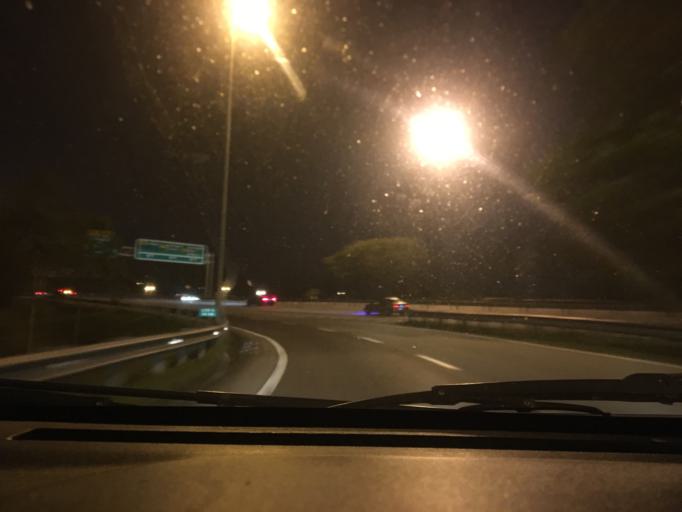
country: MY
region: Selangor
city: Kampong Baharu Balakong
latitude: 2.9805
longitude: 101.7342
